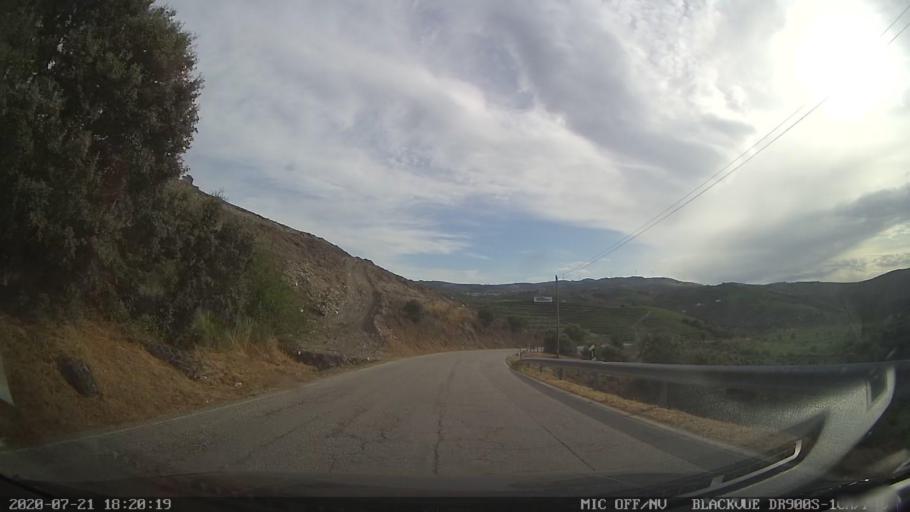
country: PT
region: Guarda
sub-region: Vila Nova de Foz Coa
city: Custoias
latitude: 41.0884
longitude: -7.3797
